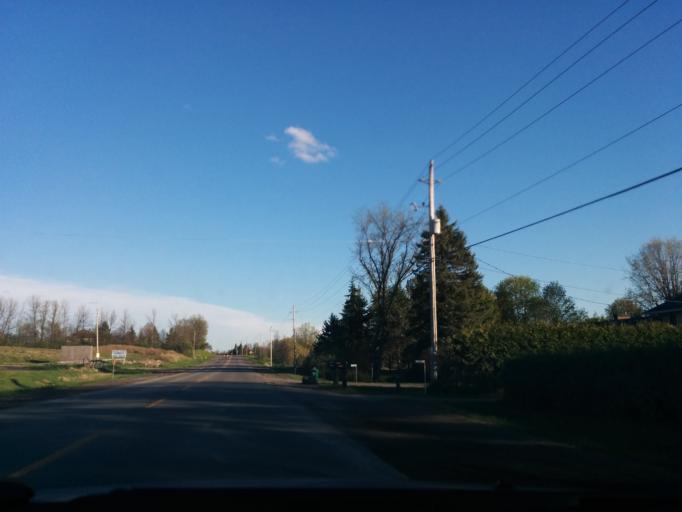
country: CA
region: Ontario
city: Bells Corners
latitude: 45.2252
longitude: -75.6676
